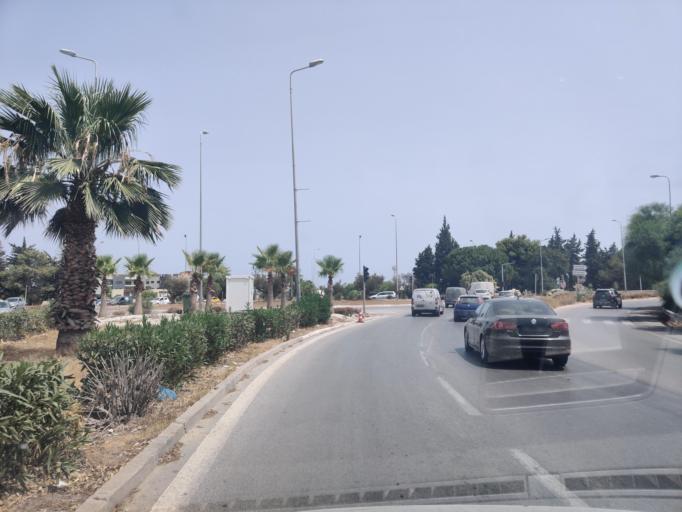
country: TN
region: Tunis
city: Carthage
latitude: 36.8582
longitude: 10.3125
